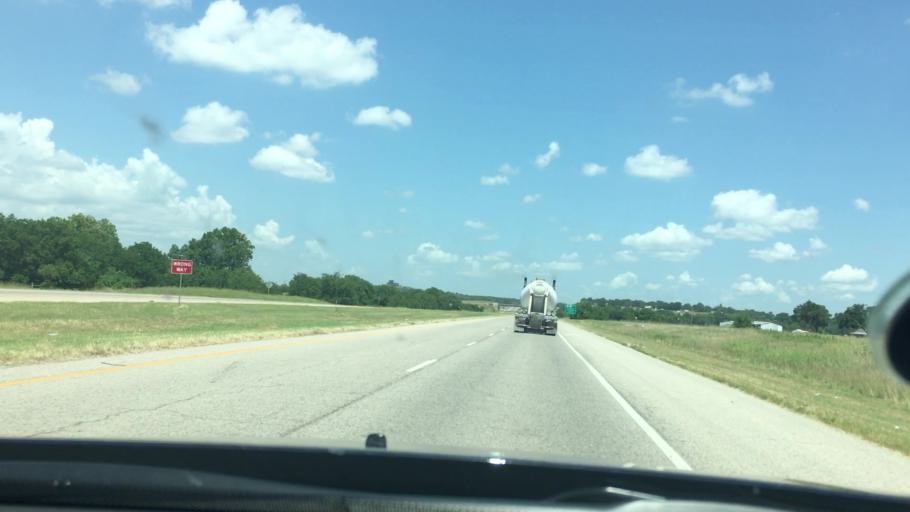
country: US
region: Oklahoma
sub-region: Pontotoc County
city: Ada
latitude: 34.7193
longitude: -96.6268
